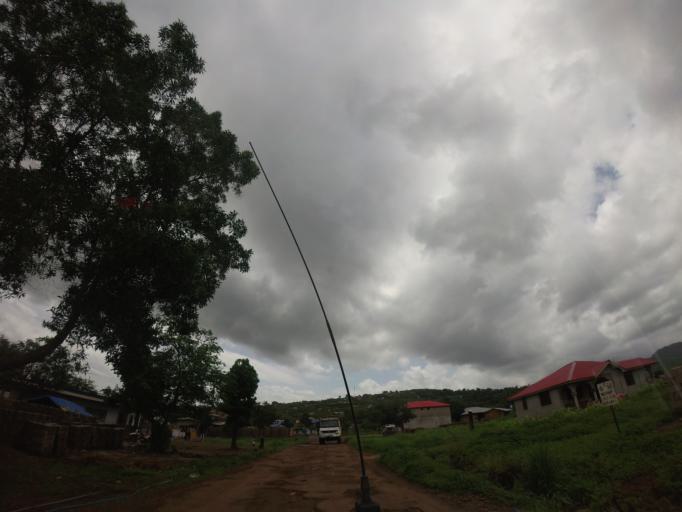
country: SL
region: Western Area
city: Hastings
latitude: 8.3825
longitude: -13.1295
